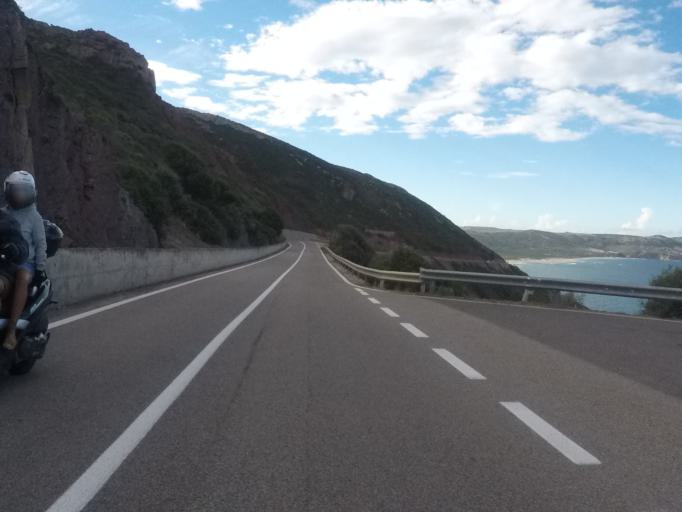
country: IT
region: Sardinia
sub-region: Provincia di Carbonia-Iglesias
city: Gonnesa
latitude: 39.3047
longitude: 8.4361
